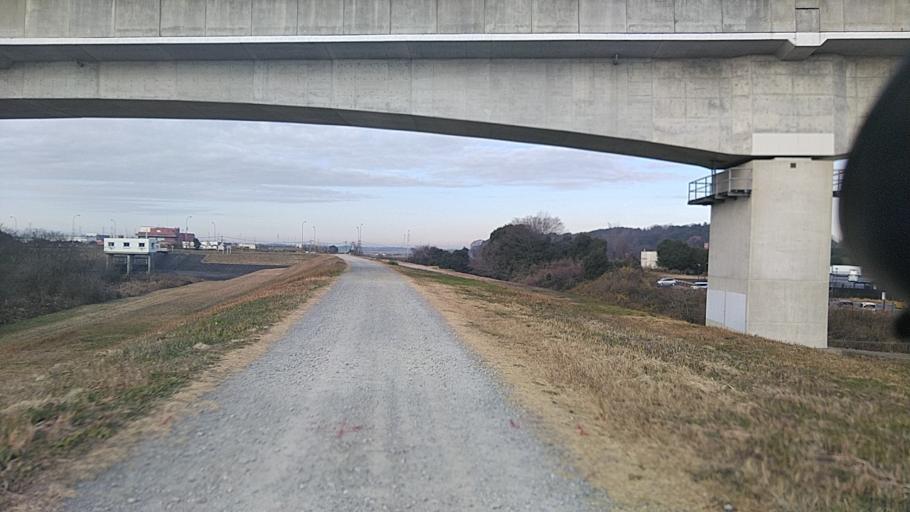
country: JP
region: Ibaraki
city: Moriya
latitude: 35.9371
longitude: 139.9703
